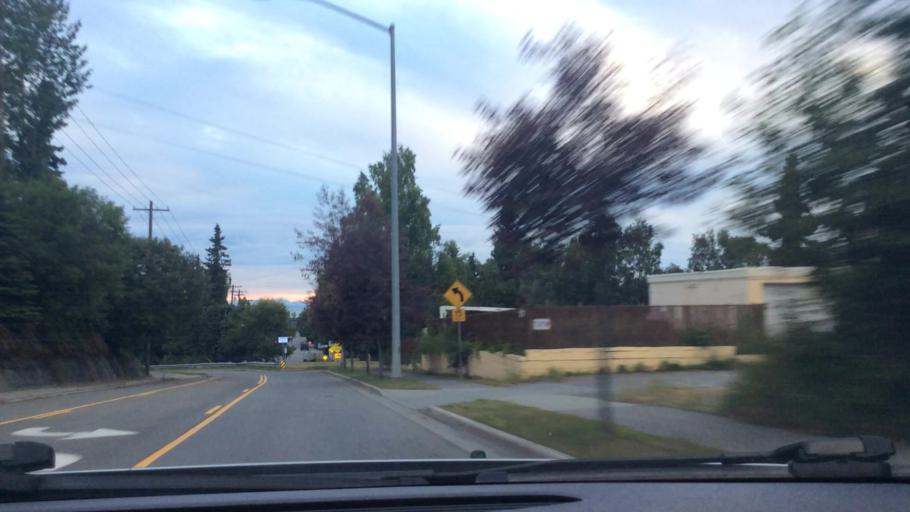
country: US
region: Alaska
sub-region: Anchorage Municipality
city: Anchorage
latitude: 61.2077
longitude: -149.9022
